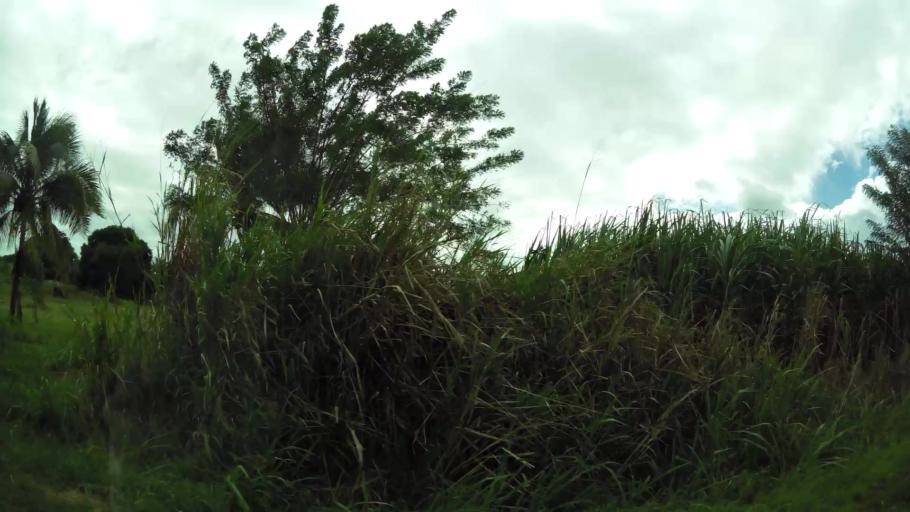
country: GP
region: Guadeloupe
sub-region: Guadeloupe
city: Sainte-Rose
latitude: 16.3235
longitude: -61.6975
